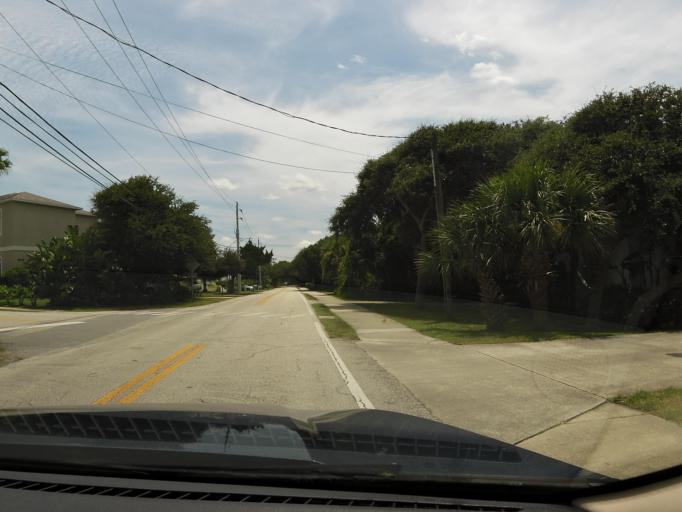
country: US
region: Florida
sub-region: Volusia County
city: Ponce Inlet
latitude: 29.0971
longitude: -80.9396
